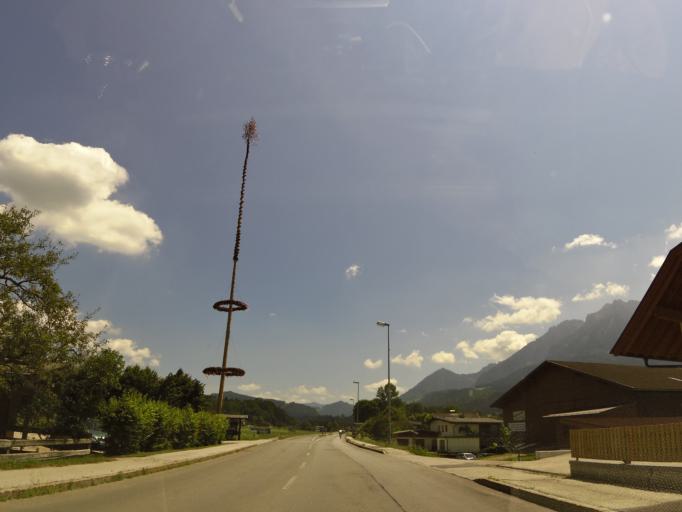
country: AT
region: Tyrol
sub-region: Politischer Bezirk Kufstein
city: Niederndorf
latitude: 47.6493
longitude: 12.2187
